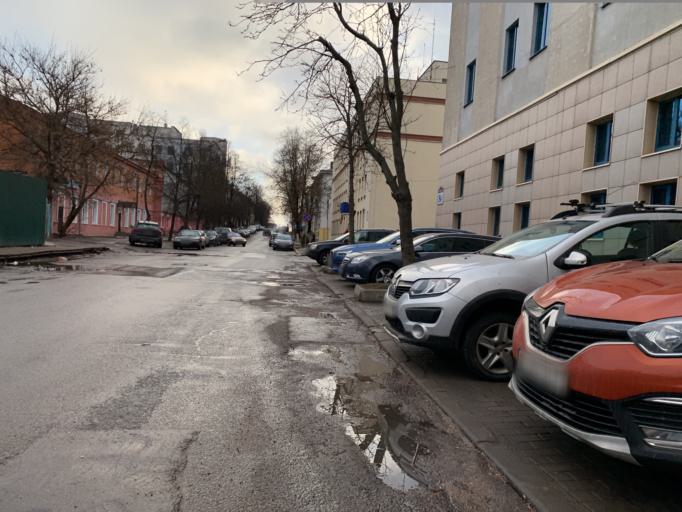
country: BY
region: Minsk
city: Minsk
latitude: 53.8892
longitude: 27.5367
